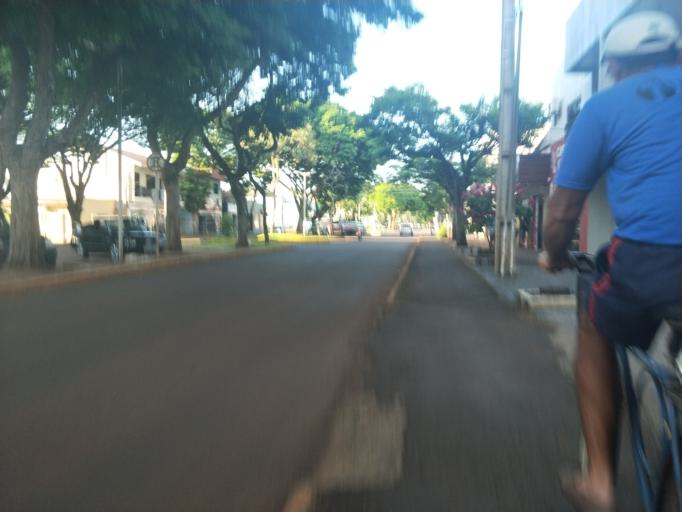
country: BR
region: Parana
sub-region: Marechal Candido Rondon
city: Marechal Candido Rondon
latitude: -24.5546
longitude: -54.0558
